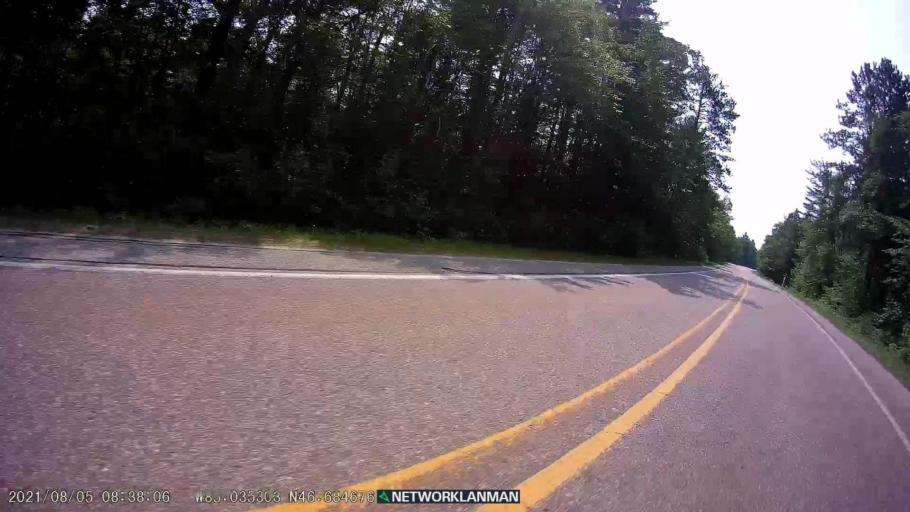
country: US
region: Michigan
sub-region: Luce County
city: Newberry
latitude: 46.6841
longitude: -85.0352
